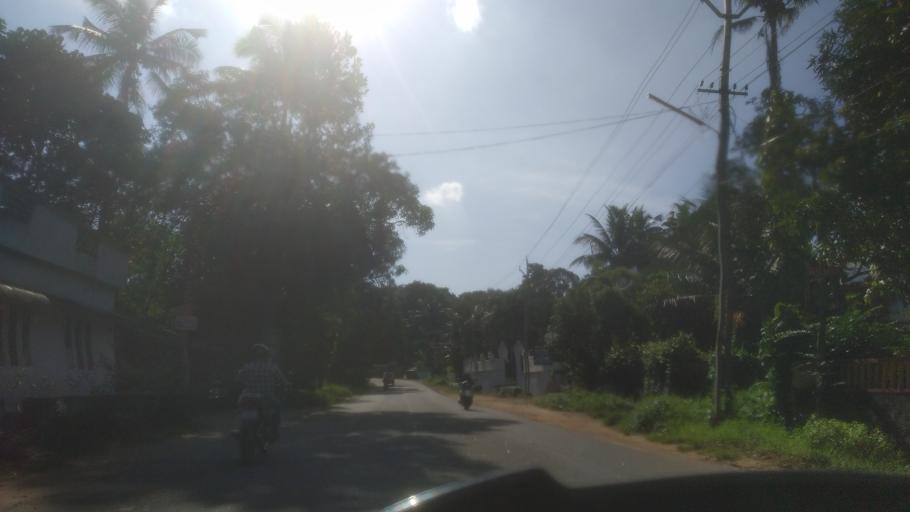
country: IN
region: Kerala
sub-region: Ernakulam
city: Muvattupuzha
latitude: 9.9822
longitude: 76.5579
